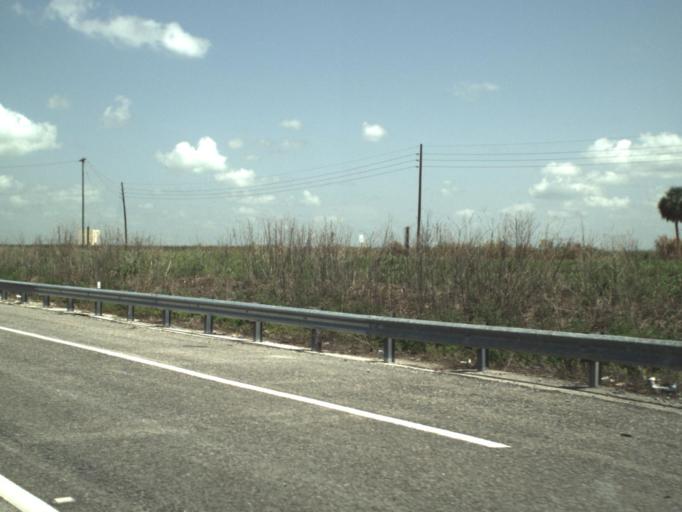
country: US
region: Florida
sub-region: Broward County
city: Coral Springs
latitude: 26.3700
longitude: -80.5648
